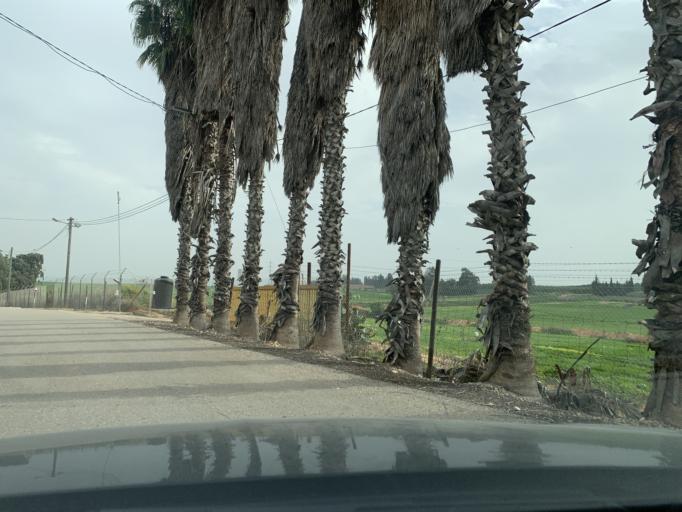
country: IL
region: Central District
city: Tirah
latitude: 32.2143
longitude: 34.9381
